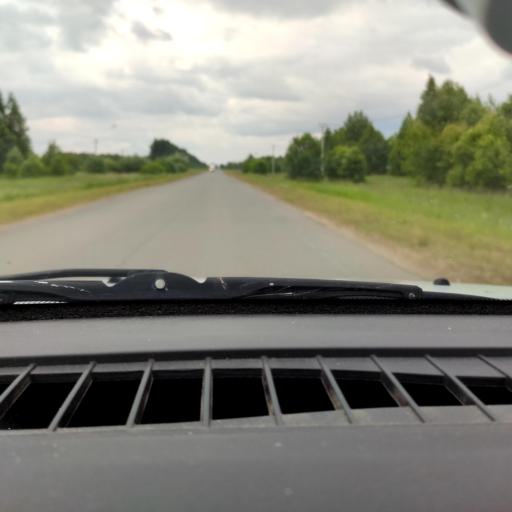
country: RU
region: Perm
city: Uinskoye
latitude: 57.1119
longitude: 56.6655
